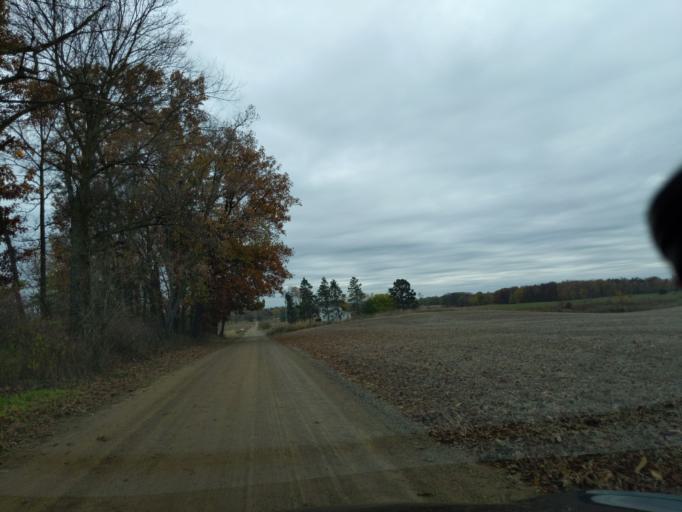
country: US
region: Michigan
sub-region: Eaton County
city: Eaton Rapids
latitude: 42.4300
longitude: -84.6005
